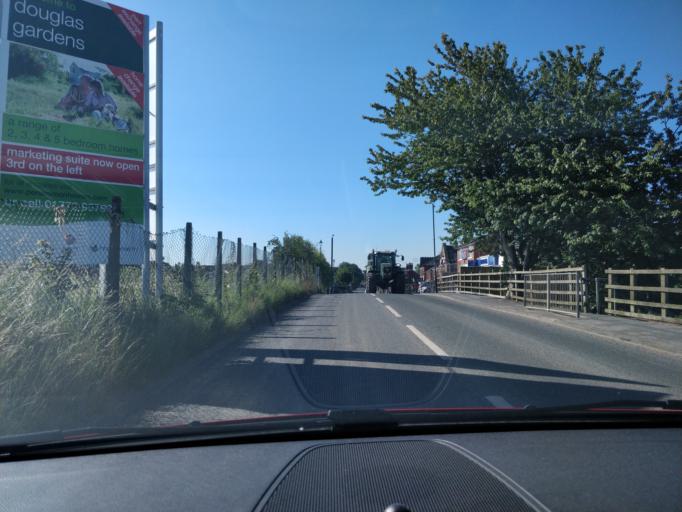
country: GB
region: England
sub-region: Lancashire
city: Tarleton
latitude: 53.6991
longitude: -2.8388
